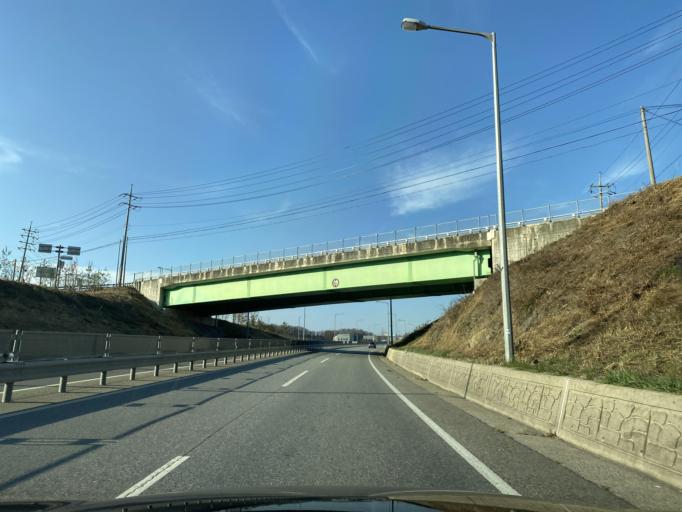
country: KR
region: Chungcheongnam-do
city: Asan
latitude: 36.7657
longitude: 126.9484
